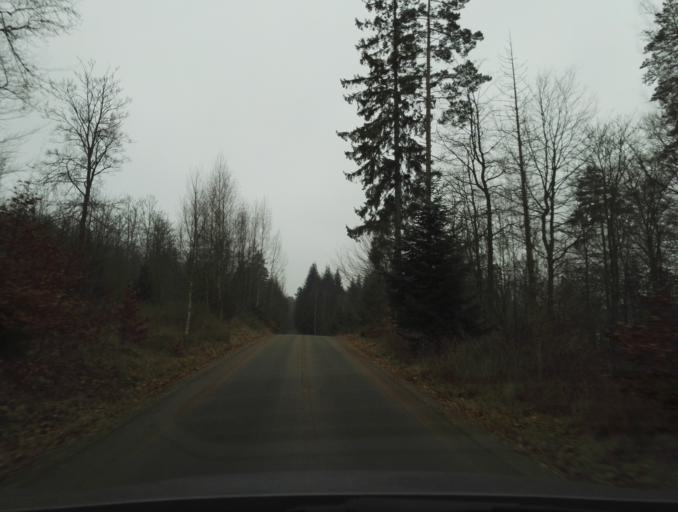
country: SE
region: Kronoberg
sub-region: Vaxjo Kommun
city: Vaexjoe
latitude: 56.9475
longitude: 14.7970
